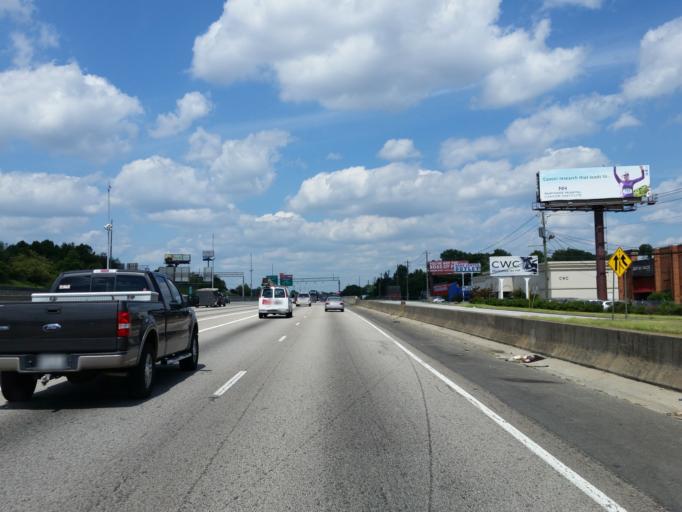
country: US
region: Georgia
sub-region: DeKalb County
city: Doraville
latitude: 33.8973
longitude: -84.2498
